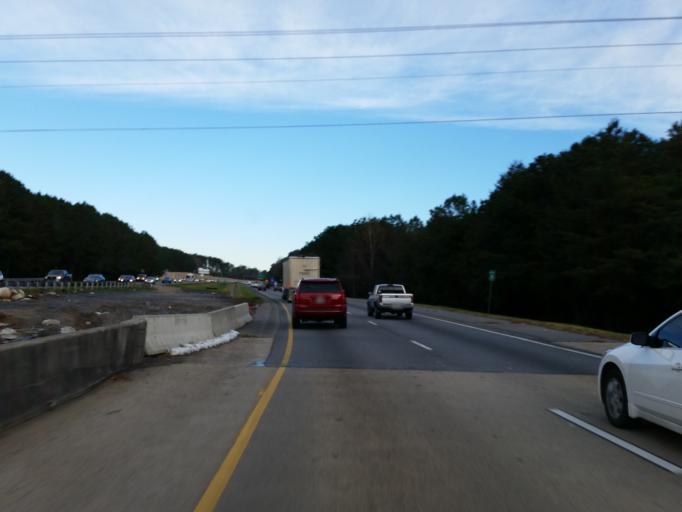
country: US
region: Georgia
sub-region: Cherokee County
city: Woodstock
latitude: 34.1025
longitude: -84.5306
